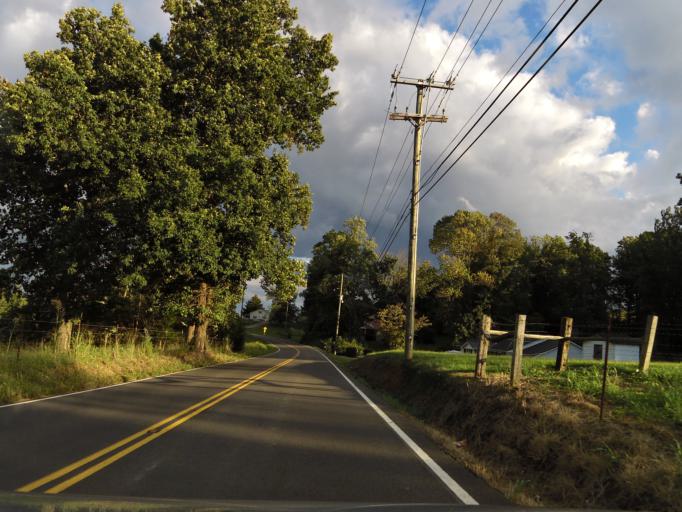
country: US
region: Tennessee
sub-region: Jefferson County
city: Jefferson City
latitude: 36.1939
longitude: -83.4987
